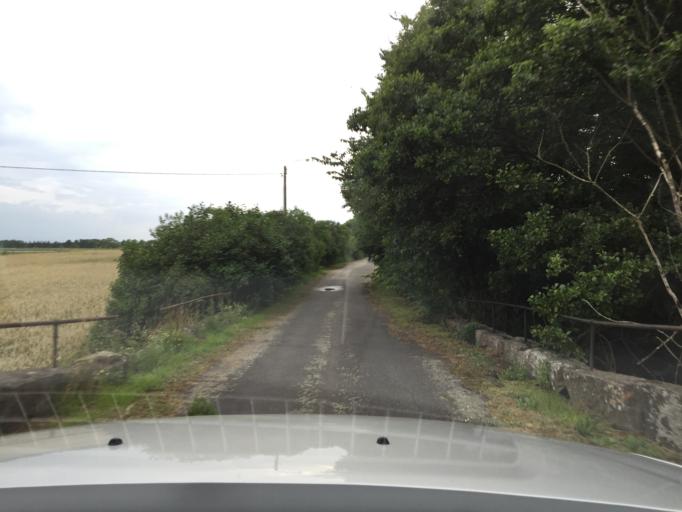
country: SE
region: Skane
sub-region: Kristianstads Kommun
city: Norra Asum
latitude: 55.9381
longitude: 14.0739
